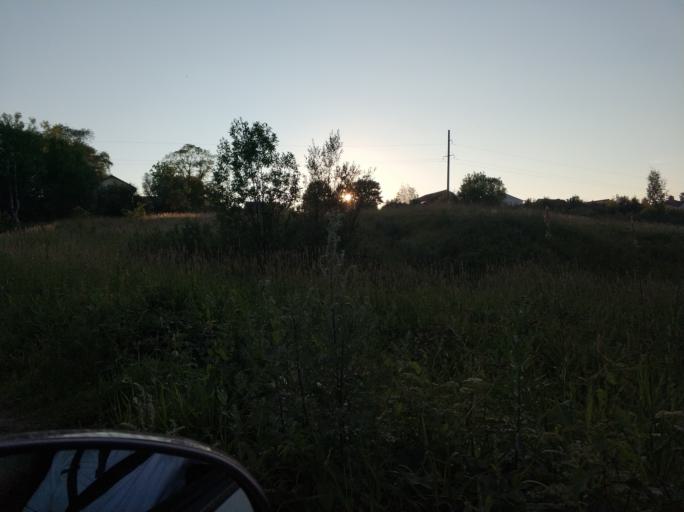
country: RU
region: St.-Petersburg
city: Gorelovo
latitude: 59.7528
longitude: 30.1148
